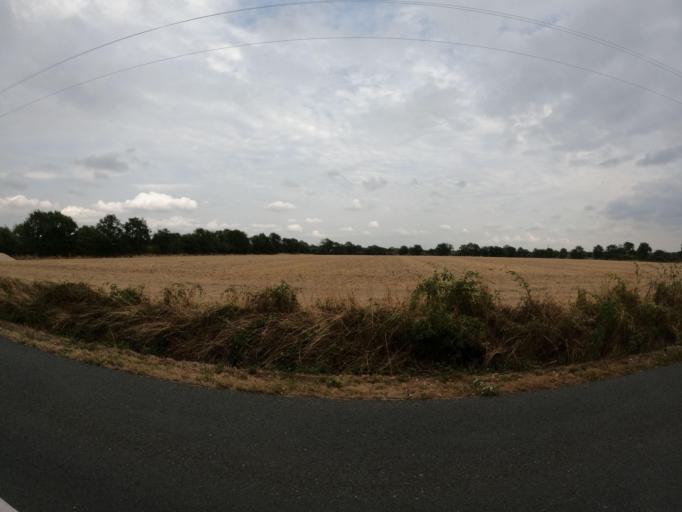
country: FR
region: Pays de la Loire
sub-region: Departement de Maine-et-Loire
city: La Romagne
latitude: 47.0527
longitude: -1.0286
